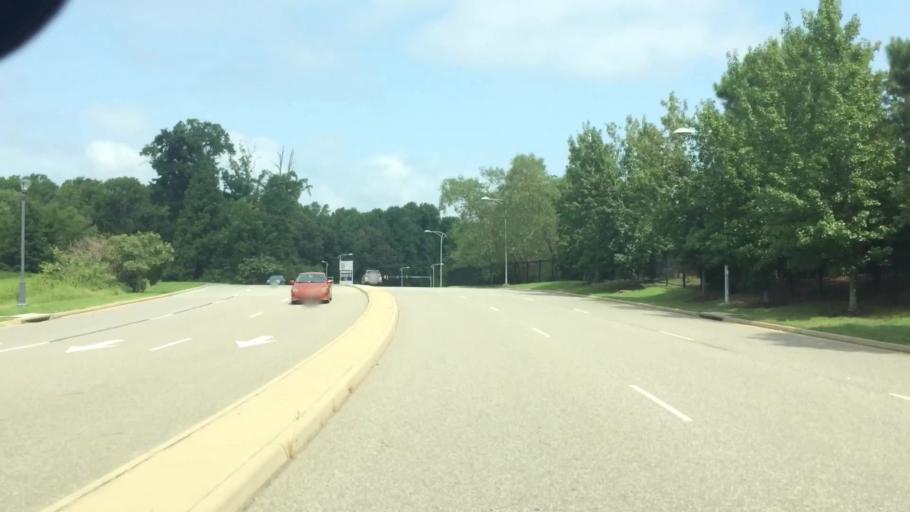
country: US
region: Virginia
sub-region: City of Williamsburg
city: Williamsburg
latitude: 37.2604
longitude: -76.6403
